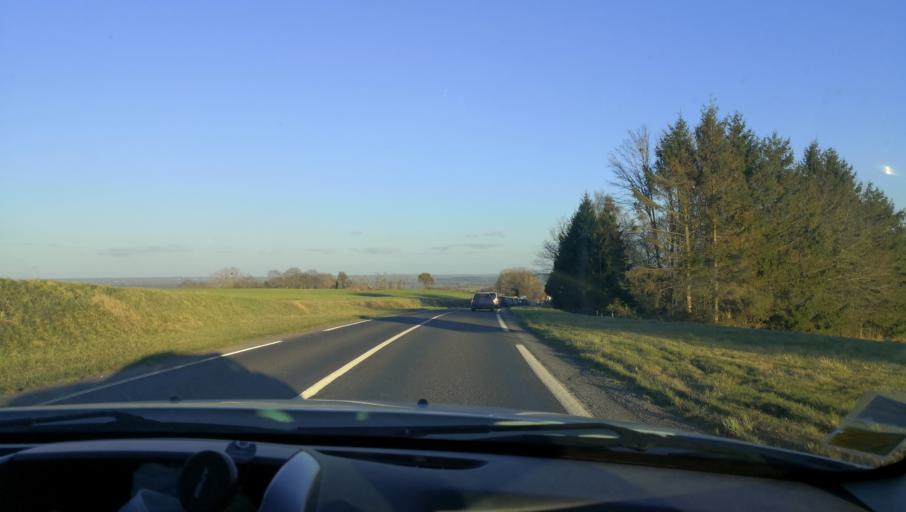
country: FR
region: Haute-Normandie
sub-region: Departement de la Seine-Maritime
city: Buchy
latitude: 49.5939
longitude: 1.4405
